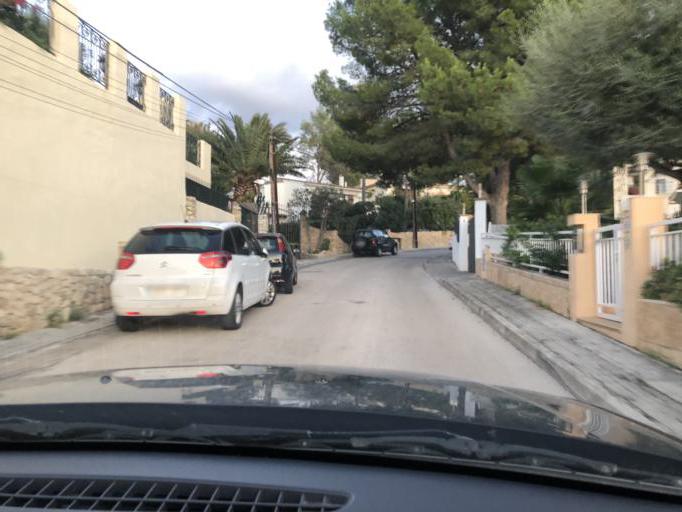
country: ES
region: Balearic Islands
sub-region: Illes Balears
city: Santa Ponsa
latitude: 39.5265
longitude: 2.4833
